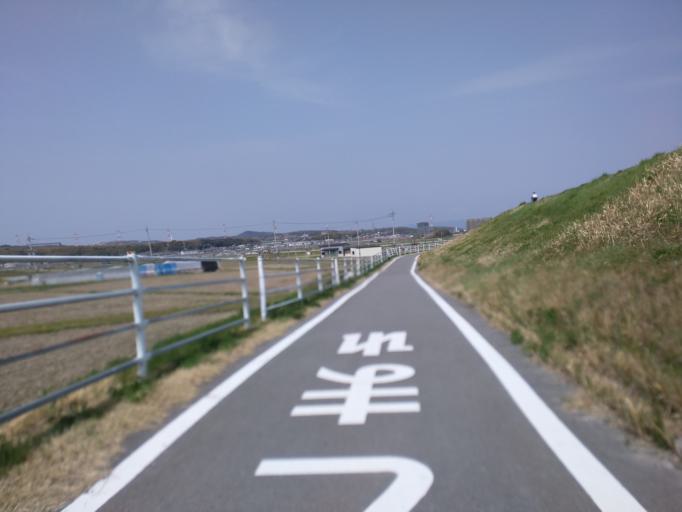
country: JP
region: Kyoto
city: Tanabe
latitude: 34.7877
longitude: 135.7977
